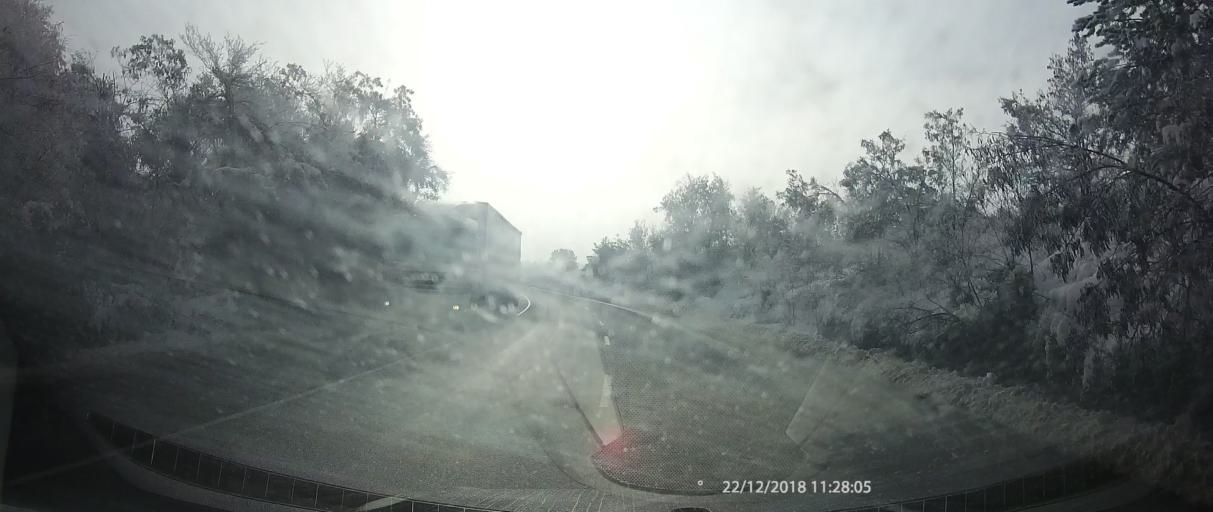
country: BG
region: Kyustendil
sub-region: Obshtina Bobovdol
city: Bobovdol
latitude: 42.2714
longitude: 22.9427
